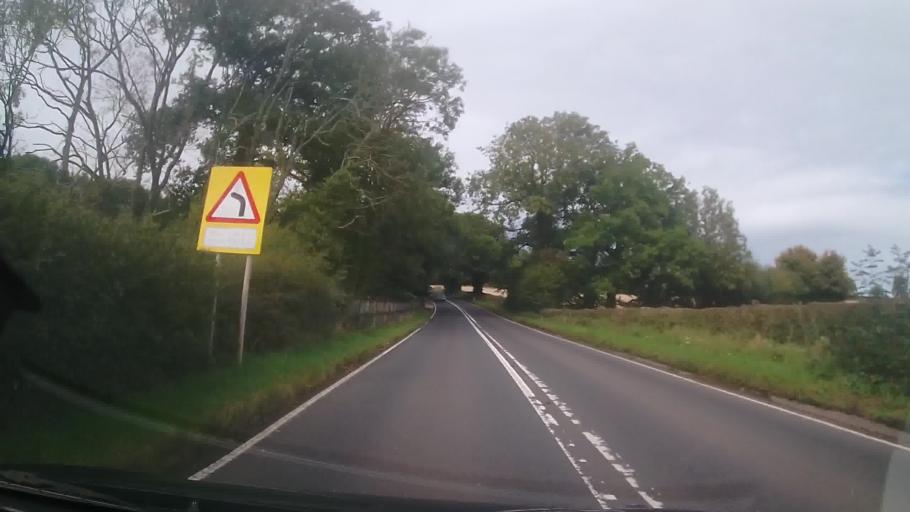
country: GB
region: England
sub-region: Shropshire
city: Romsley
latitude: 52.4343
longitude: -2.3152
